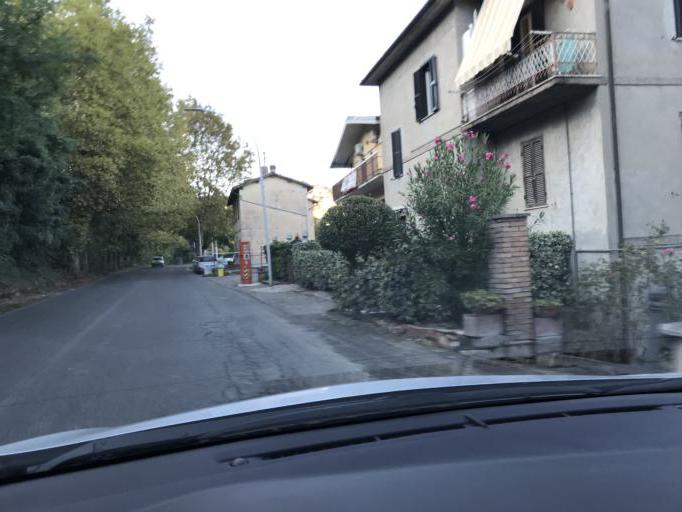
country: IT
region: Latium
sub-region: Provincia di Viterbo
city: Orte
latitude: 42.4536
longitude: 12.3879
